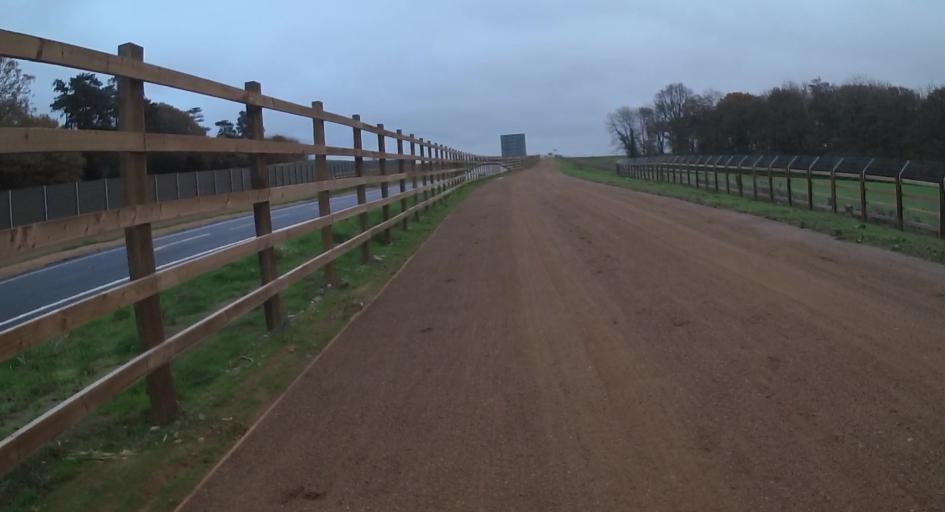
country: GB
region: England
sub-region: West Berkshire
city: Arborfield
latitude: 51.3919
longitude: -0.9146
